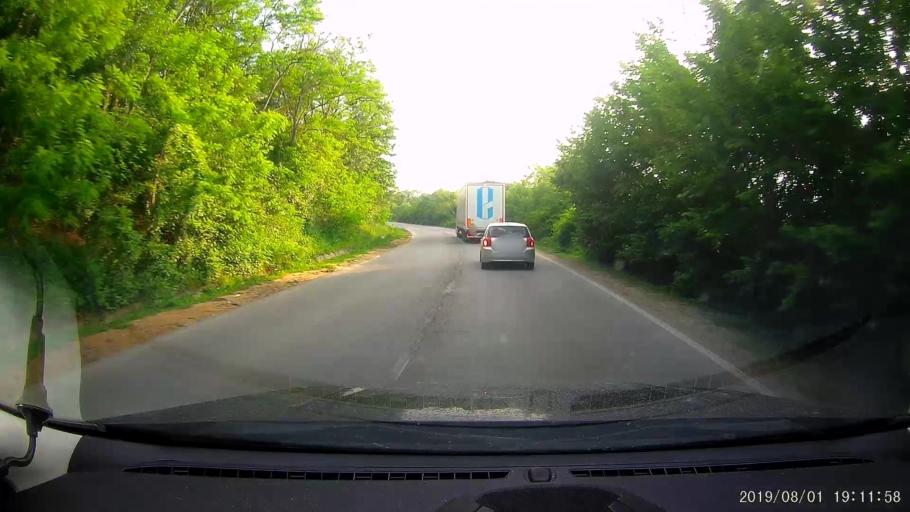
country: BG
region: Shumen
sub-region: Obshtina Smyadovo
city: Smyadovo
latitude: 42.9685
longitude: 26.9543
